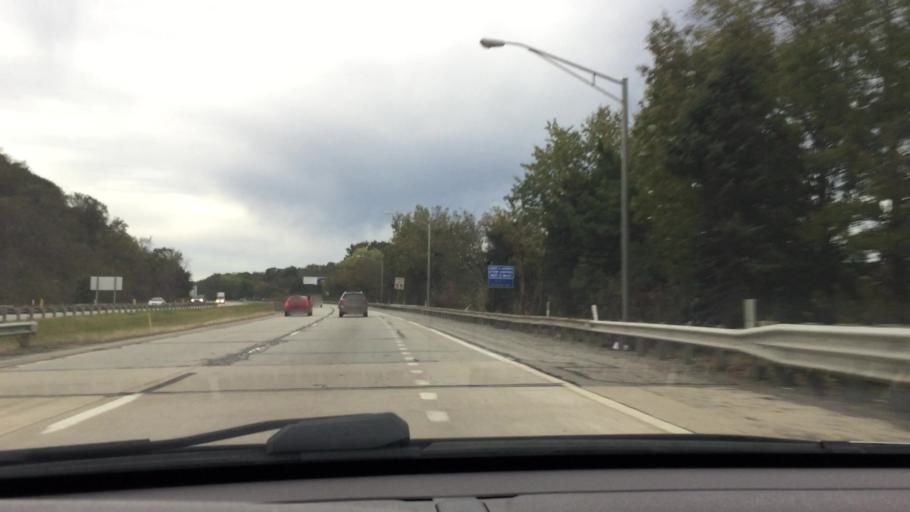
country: US
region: Pennsylvania
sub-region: Beaver County
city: Aliquippa
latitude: 40.6044
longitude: -80.3027
